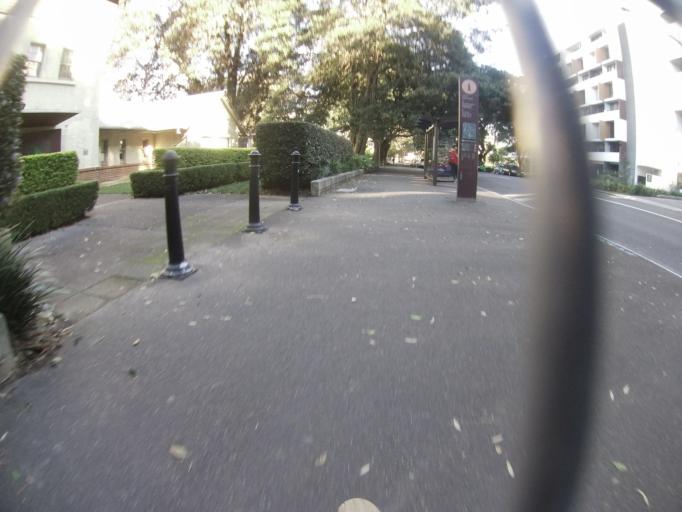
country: AU
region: New South Wales
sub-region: City of Sydney
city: Alexandria
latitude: -33.9051
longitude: 151.2092
